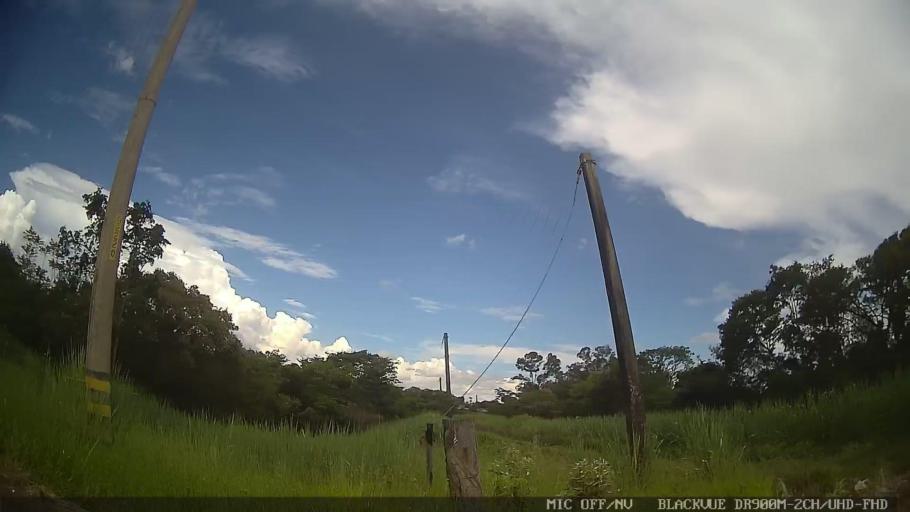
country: BR
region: Sao Paulo
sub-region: Conchas
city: Conchas
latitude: -23.0076
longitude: -48.0036
